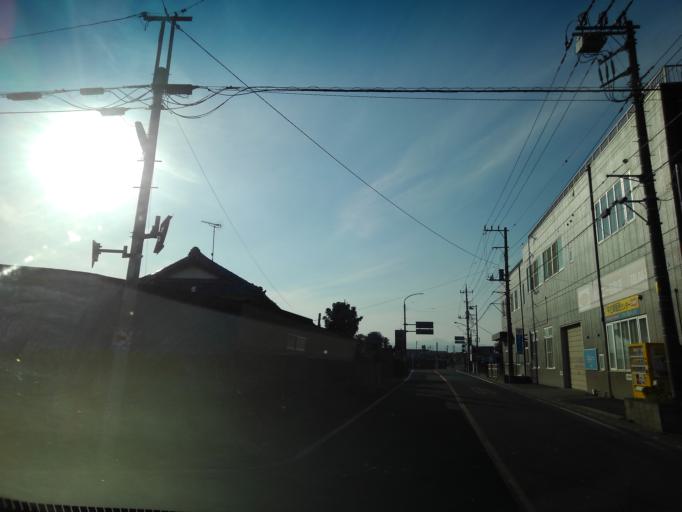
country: JP
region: Tokyo
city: Fussa
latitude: 35.7917
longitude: 139.3681
